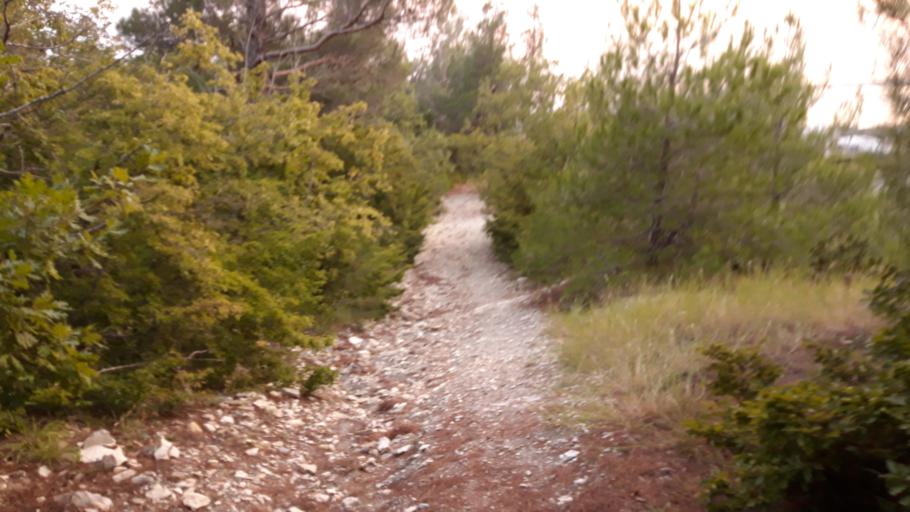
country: RU
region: Krasnodarskiy
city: Gelendzhik
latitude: 44.5809
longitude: 38.0846
